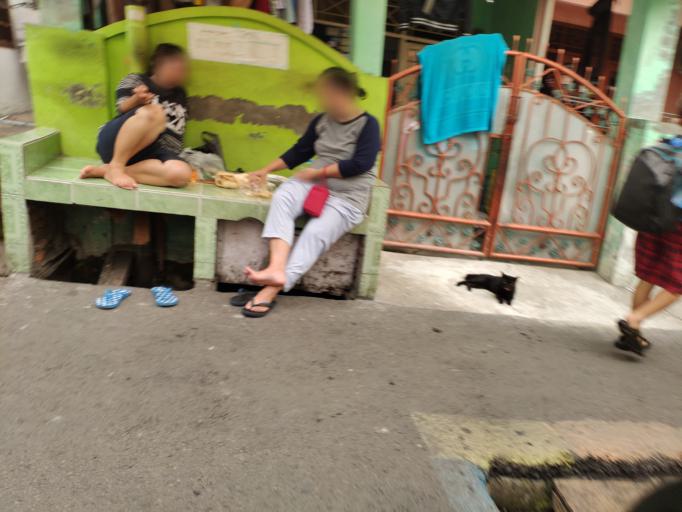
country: ID
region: Jakarta Raya
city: Jakarta
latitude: -6.1964
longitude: 106.8641
